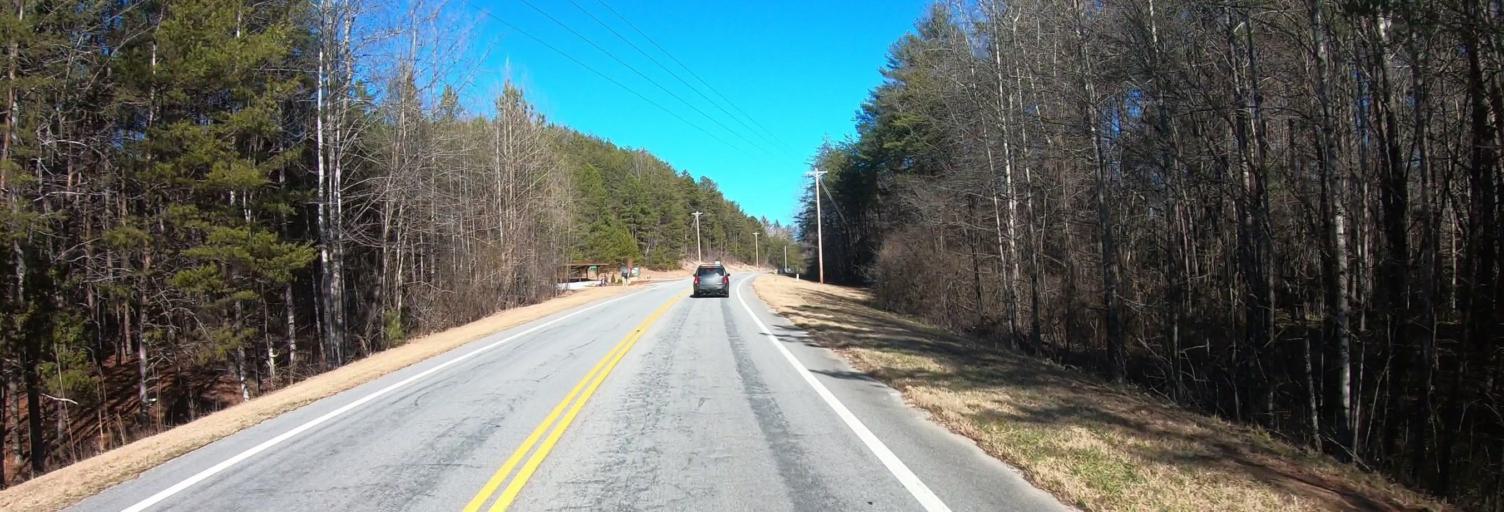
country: US
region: South Carolina
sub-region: Pickens County
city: Pickens
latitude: 34.9998
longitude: -82.7468
